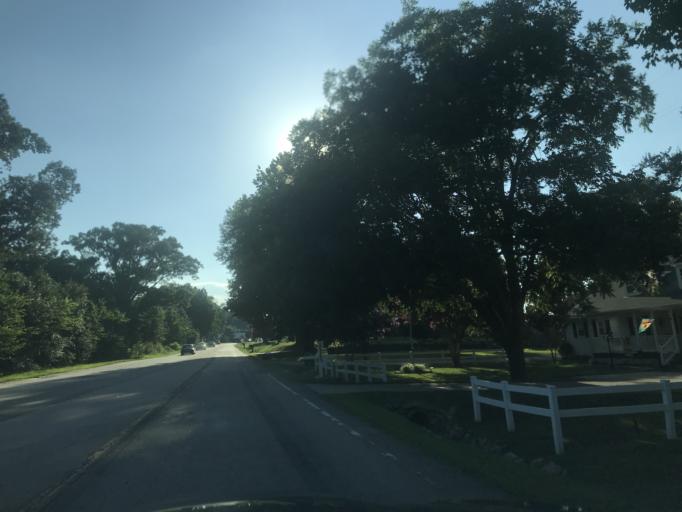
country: US
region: North Carolina
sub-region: Wake County
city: Wake Forest
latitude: 35.9181
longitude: -78.5431
